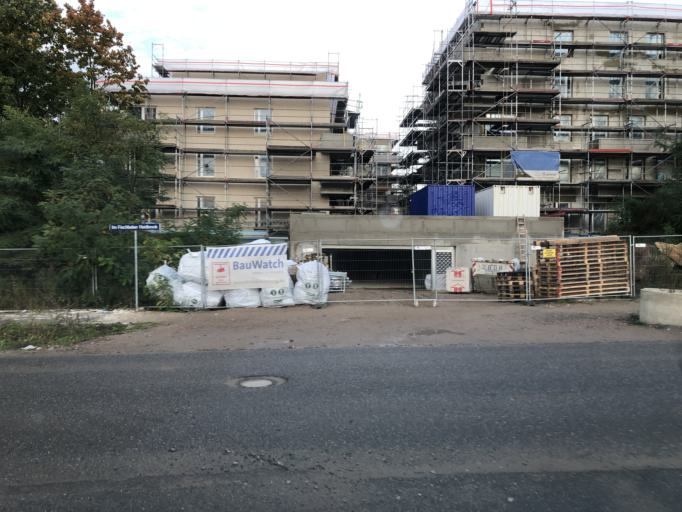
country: DE
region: Lower Saxony
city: Neu Wulmstorf
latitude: 53.4647
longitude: 9.8122
